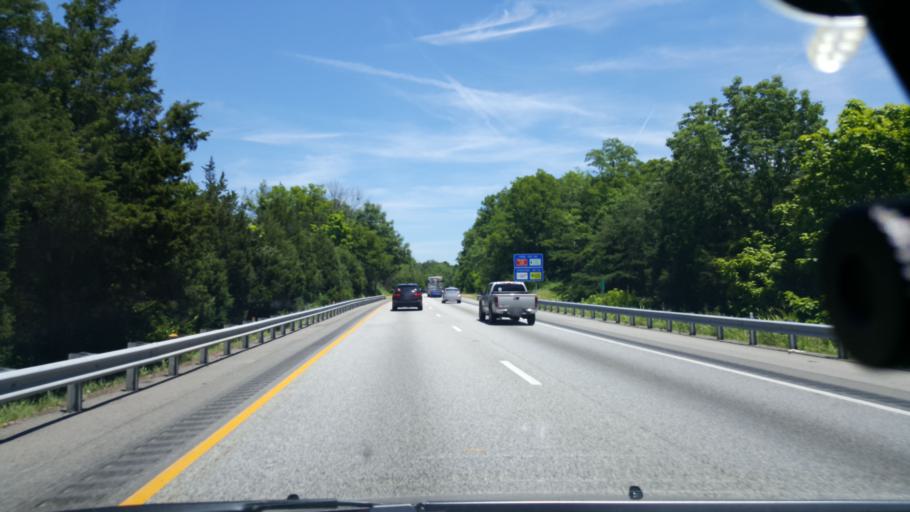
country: US
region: Virginia
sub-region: Botetourt County
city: Daleville
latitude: 37.4418
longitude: -79.8651
